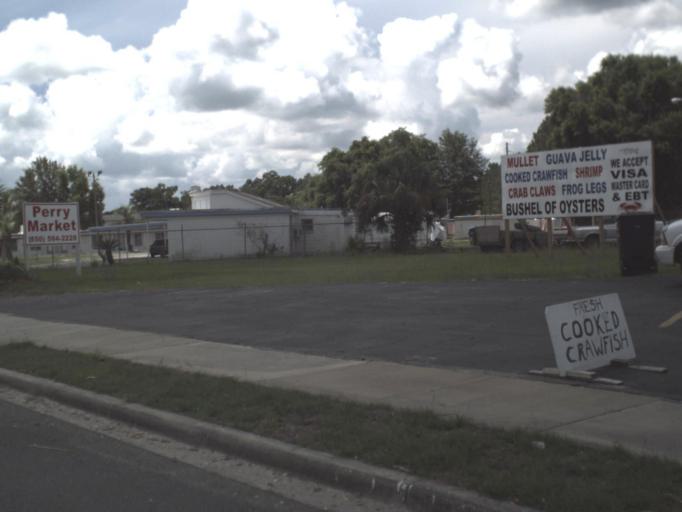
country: US
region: Florida
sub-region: Taylor County
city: Perry
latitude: 30.1019
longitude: -83.5872
